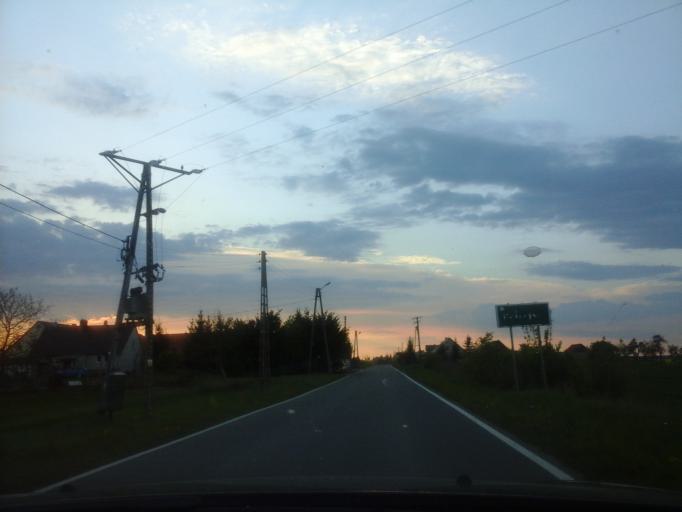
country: PL
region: West Pomeranian Voivodeship
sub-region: Powiat choszczenski
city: Pelczyce
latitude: 53.0380
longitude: 15.3216
